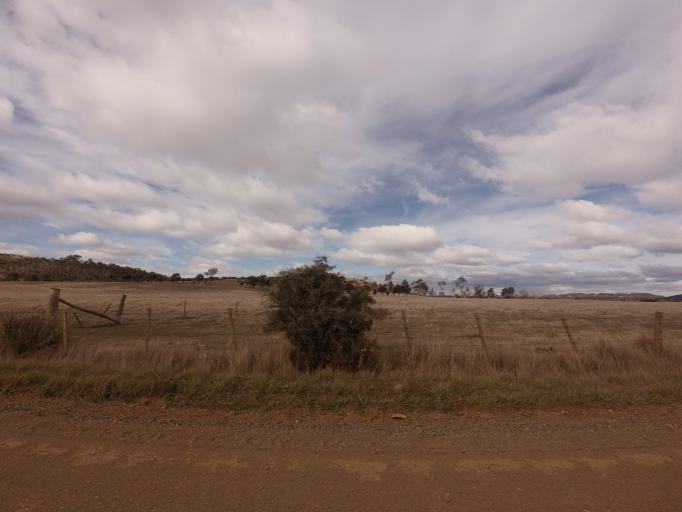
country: AU
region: Tasmania
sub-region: Brighton
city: Bridgewater
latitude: -42.4222
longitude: 147.3914
